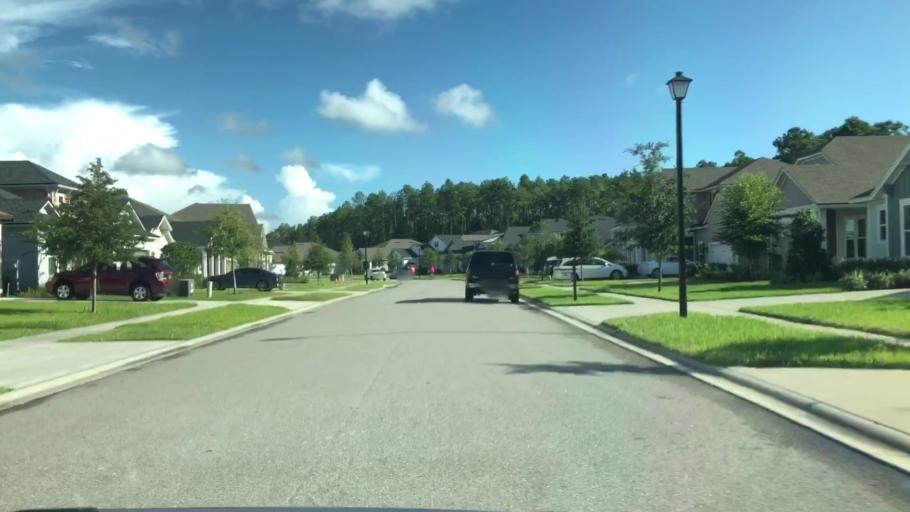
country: US
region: Florida
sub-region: Saint Johns County
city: Palm Valley
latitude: 30.1302
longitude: -81.4087
